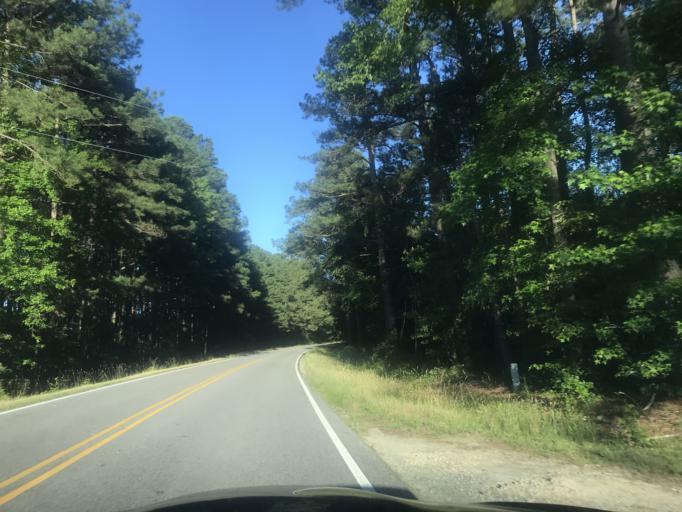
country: US
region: North Carolina
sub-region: Johnston County
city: Archer Lodge
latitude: 35.7311
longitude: -78.3975
